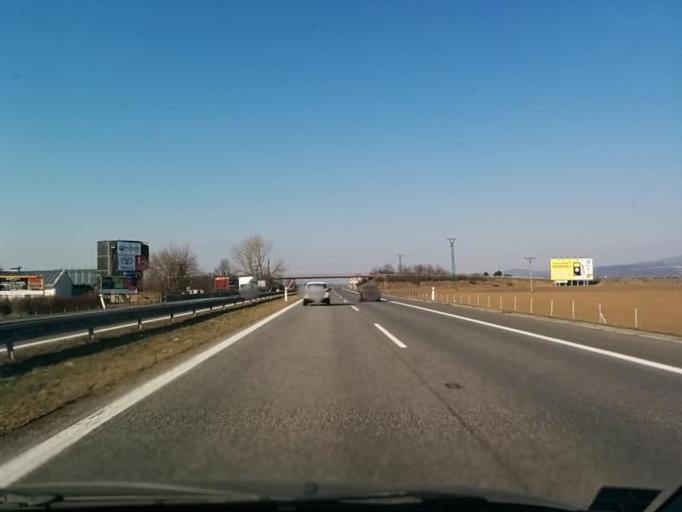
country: SK
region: Trnavsky
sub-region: Okres Trnava
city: Piestany
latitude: 48.6271
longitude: 17.8069
